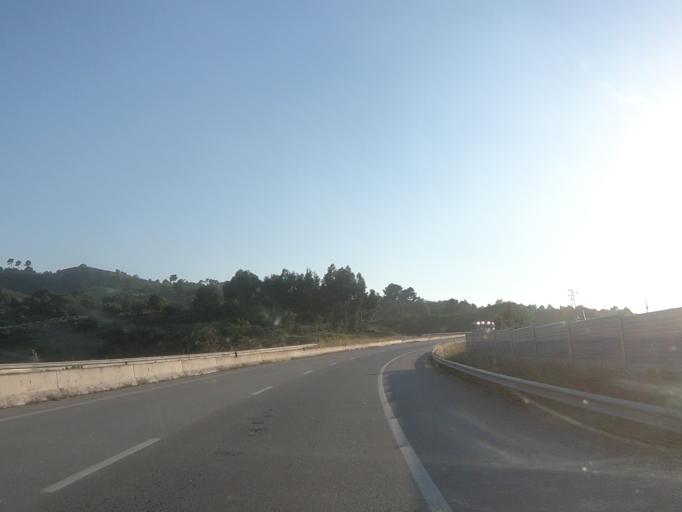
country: PT
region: Guarda
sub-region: Celorico da Beira
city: Celorico da Beira
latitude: 40.6263
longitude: -7.3648
